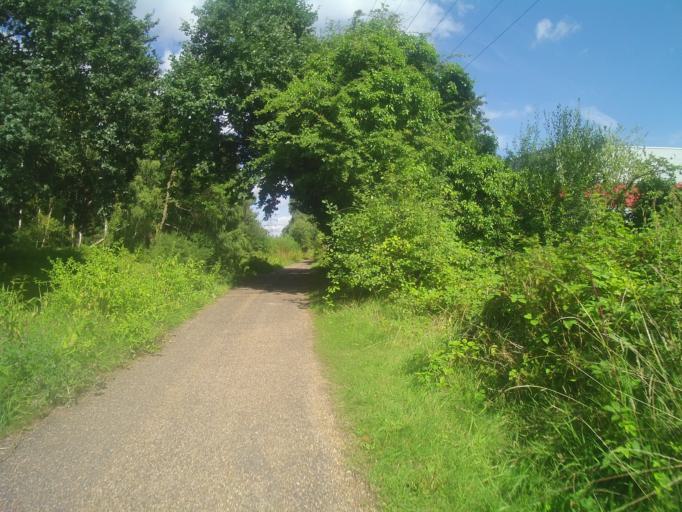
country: GB
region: England
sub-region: Surrey
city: Woking
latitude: 51.3271
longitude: -0.5472
